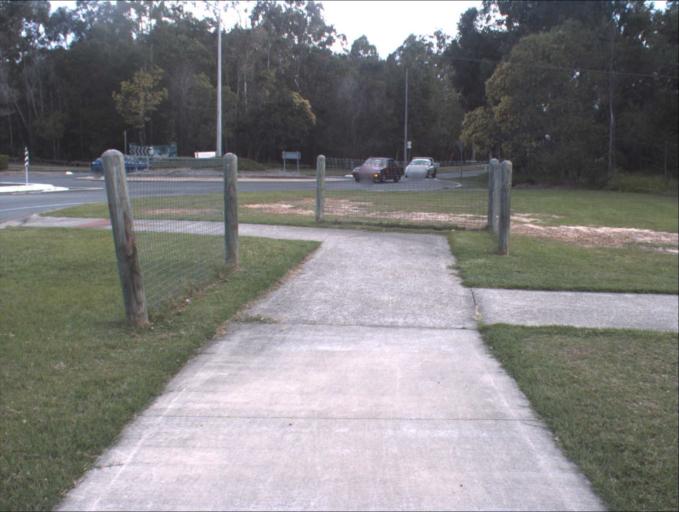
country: AU
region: Queensland
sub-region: Logan
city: Park Ridge South
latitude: -27.6850
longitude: 153.0582
